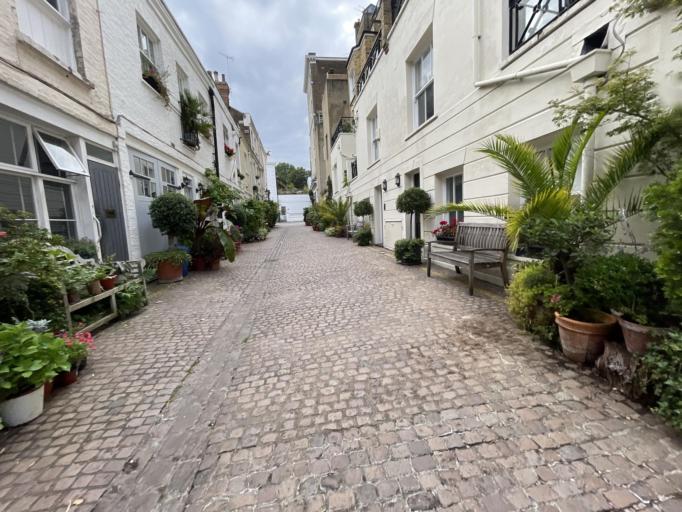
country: GB
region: England
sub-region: Greater London
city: Chelsea
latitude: 51.4932
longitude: -0.1810
